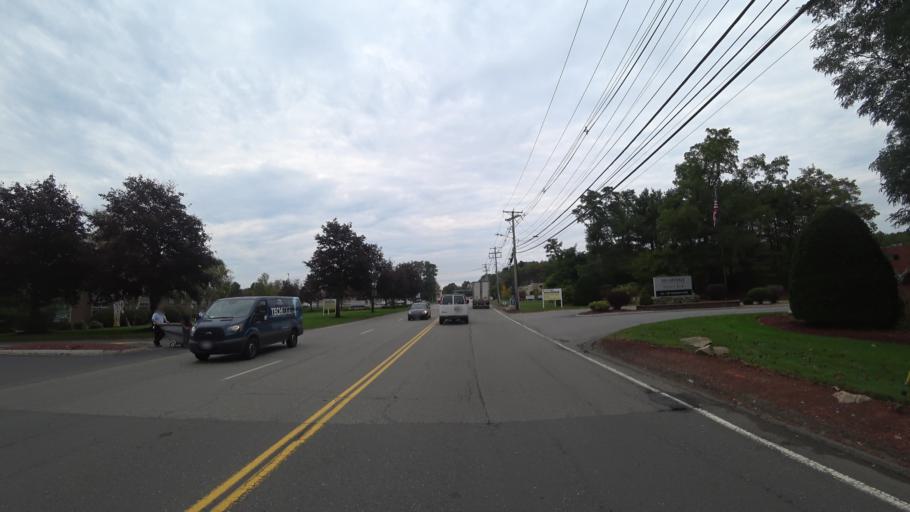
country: US
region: Massachusetts
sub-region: Middlesex County
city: Wilmington
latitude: 42.5882
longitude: -71.1565
